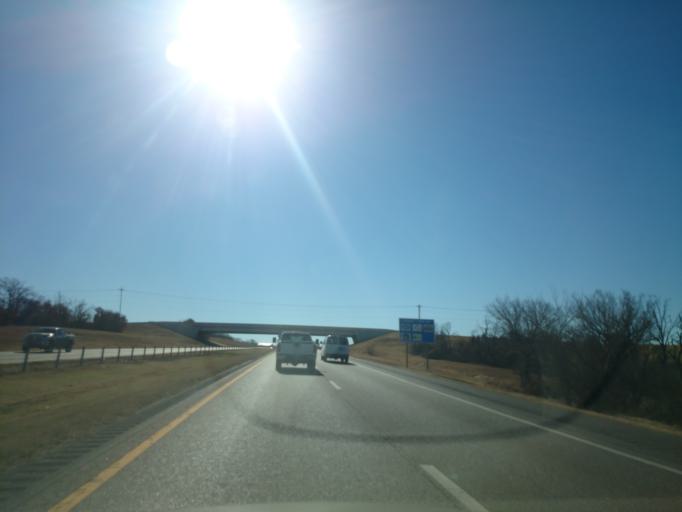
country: US
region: Oklahoma
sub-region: Oklahoma County
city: Edmond
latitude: 35.6836
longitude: -97.4164
